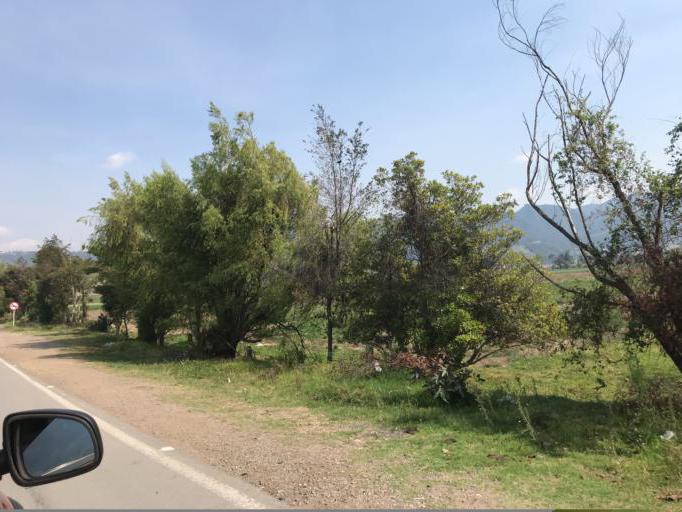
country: CO
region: Boyaca
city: Samaca
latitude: 5.5038
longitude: -73.4979
